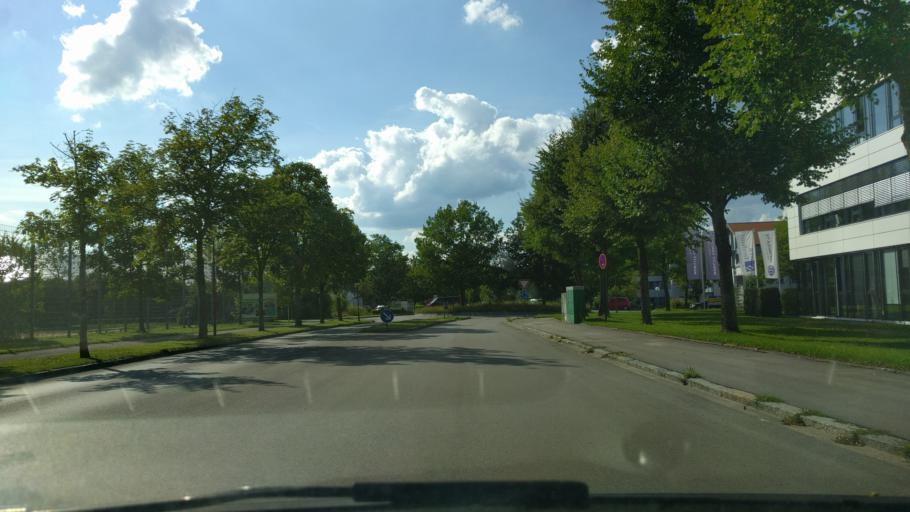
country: DE
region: Bavaria
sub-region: Upper Bavaria
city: Oberhaching
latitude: 48.0293
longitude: 11.5823
